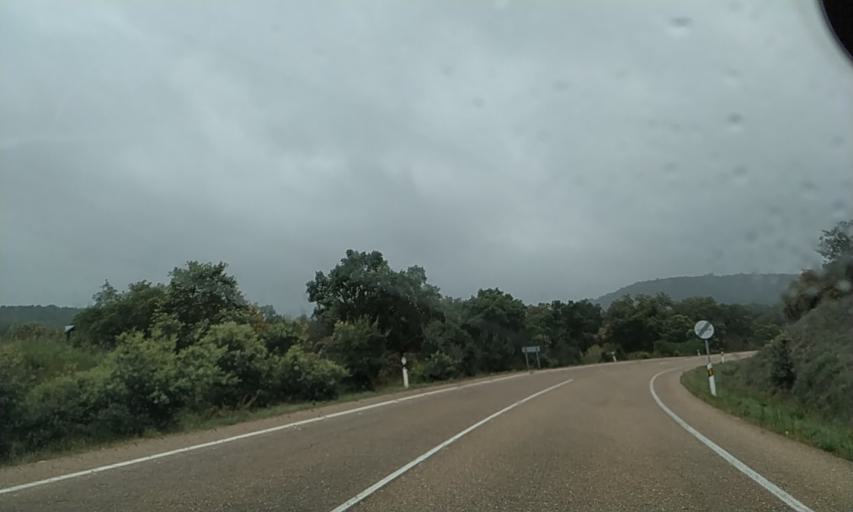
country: ES
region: Extremadura
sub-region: Provincia de Badajoz
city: Puebla de Obando
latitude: 39.2022
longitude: -6.5872
